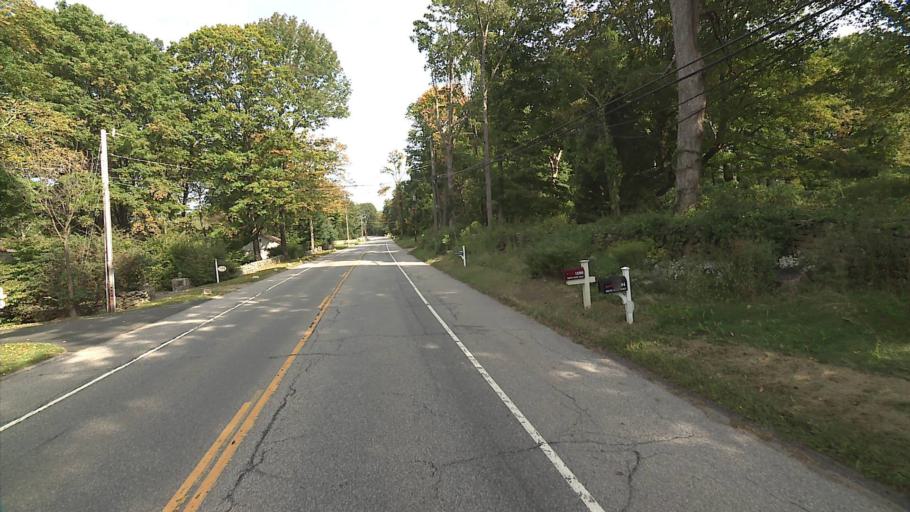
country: US
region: Connecticut
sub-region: Fairfield County
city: New Canaan
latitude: 41.1937
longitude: -73.5070
